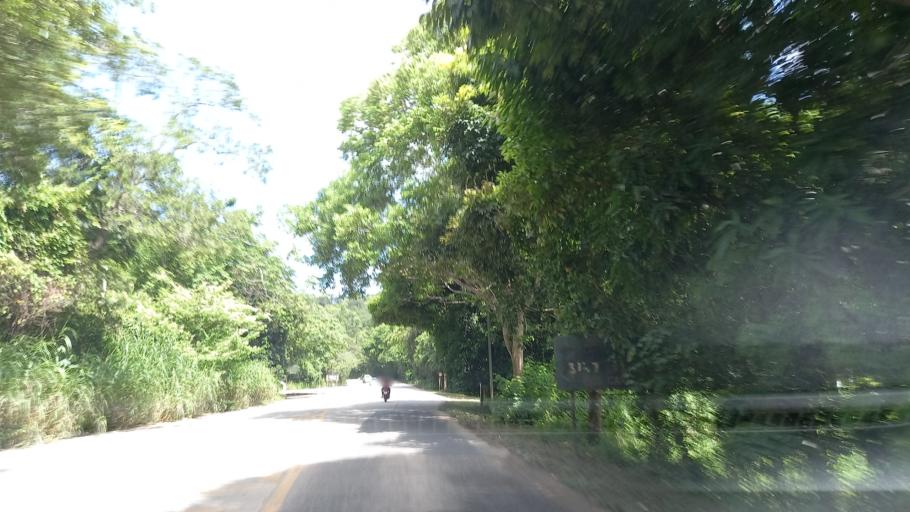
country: BR
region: Pernambuco
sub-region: Rio Formoso
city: Rio Formoso
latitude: -8.7320
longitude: -35.1736
